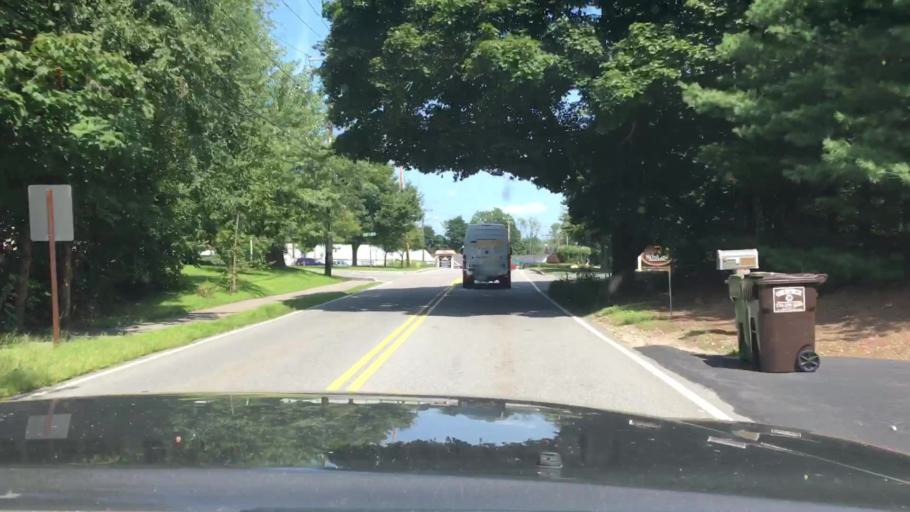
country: US
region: Massachusetts
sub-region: Middlesex County
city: Cochituate
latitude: 42.3217
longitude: -71.3560
